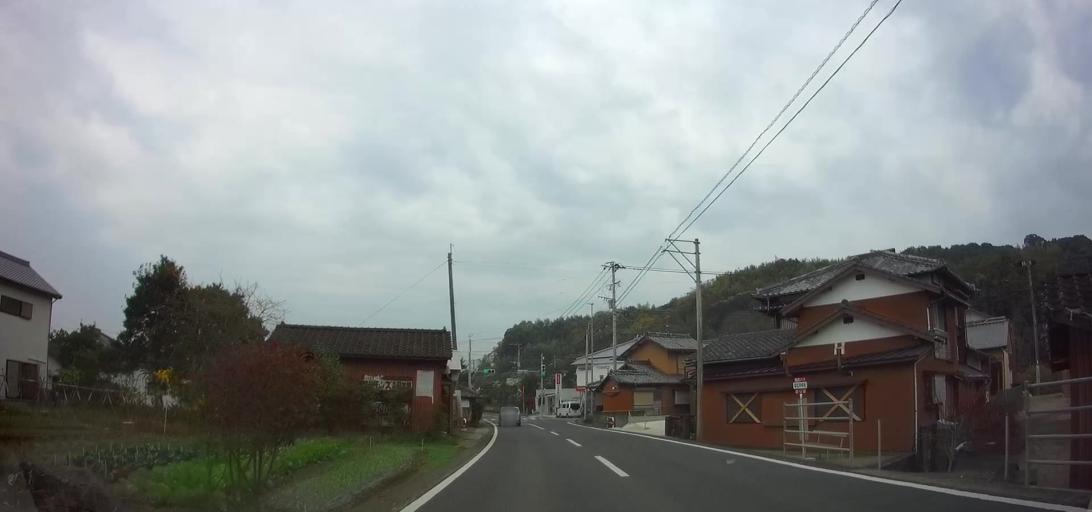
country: JP
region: Nagasaki
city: Shimabara
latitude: 32.6544
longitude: 130.2692
